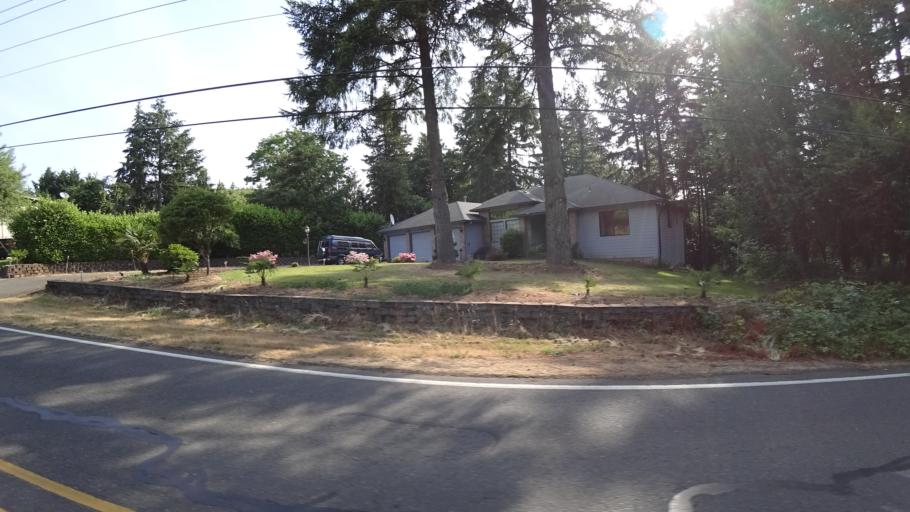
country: US
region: Oregon
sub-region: Clackamas County
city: Happy Valley
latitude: 45.4504
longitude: -122.5359
